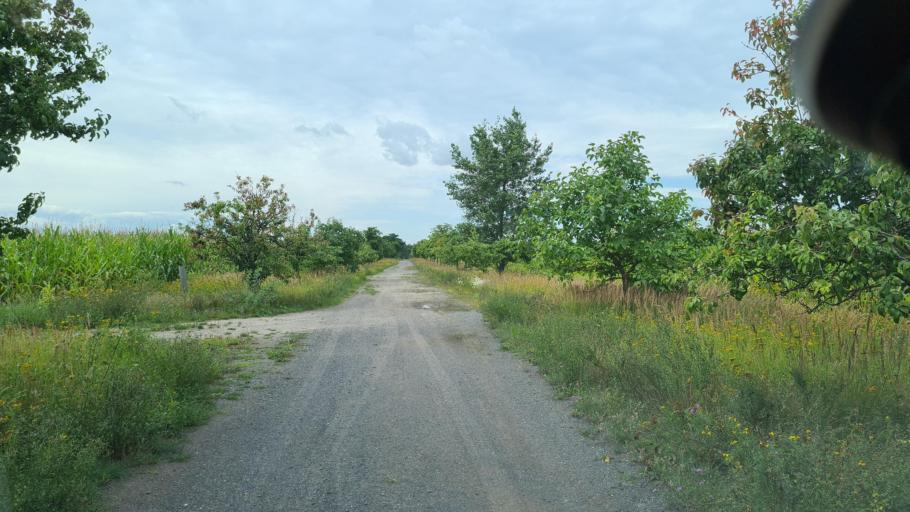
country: DE
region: Brandenburg
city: Spremberg
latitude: 51.5731
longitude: 14.2963
